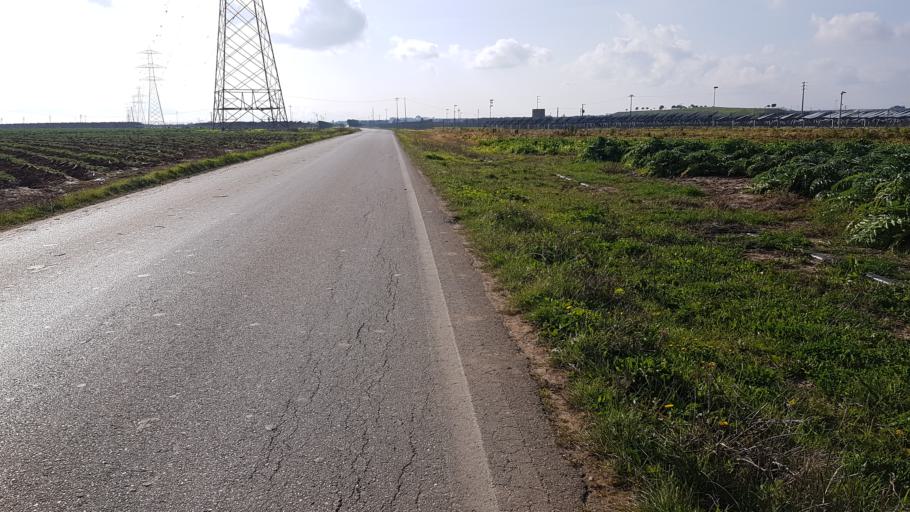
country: IT
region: Apulia
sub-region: Provincia di Brindisi
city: La Rosa
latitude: 40.5920
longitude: 17.9033
